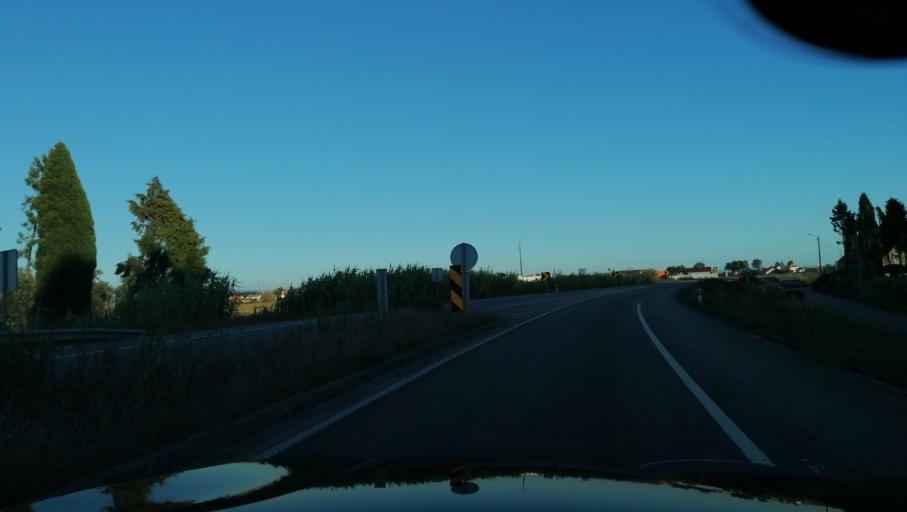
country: PT
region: Aveiro
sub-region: Aveiro
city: Oliveirinha
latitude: 40.5971
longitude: -8.6133
